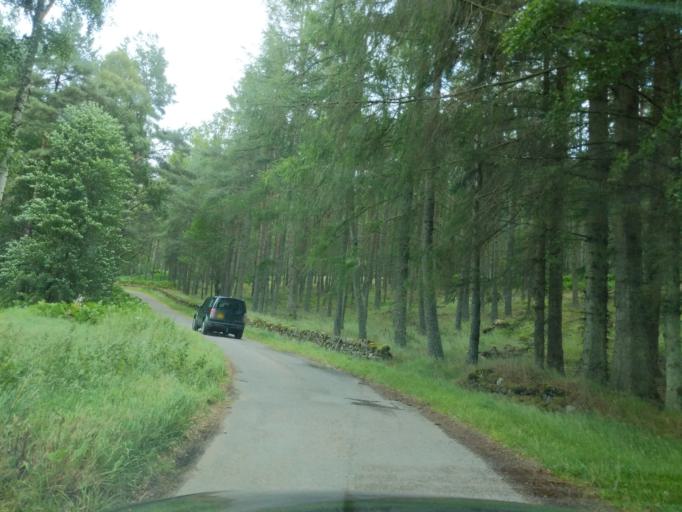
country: GB
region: Scotland
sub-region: Aberdeenshire
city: Aboyne
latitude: 57.0552
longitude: -2.7532
